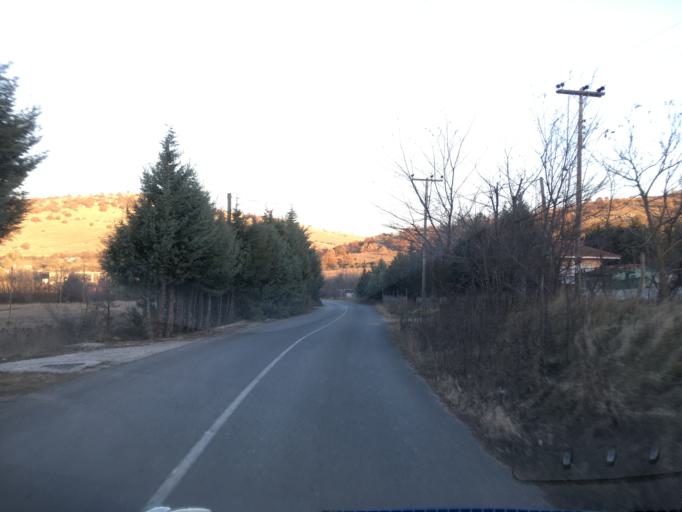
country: GR
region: West Macedonia
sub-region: Nomos Kozanis
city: Koila
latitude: 40.3288
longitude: 21.8055
